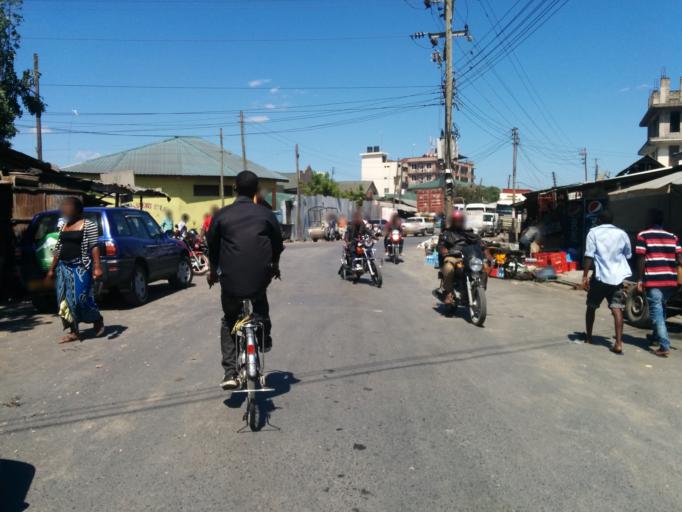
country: TZ
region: Dar es Salaam
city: Magomeni
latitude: -6.7969
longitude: 39.2336
